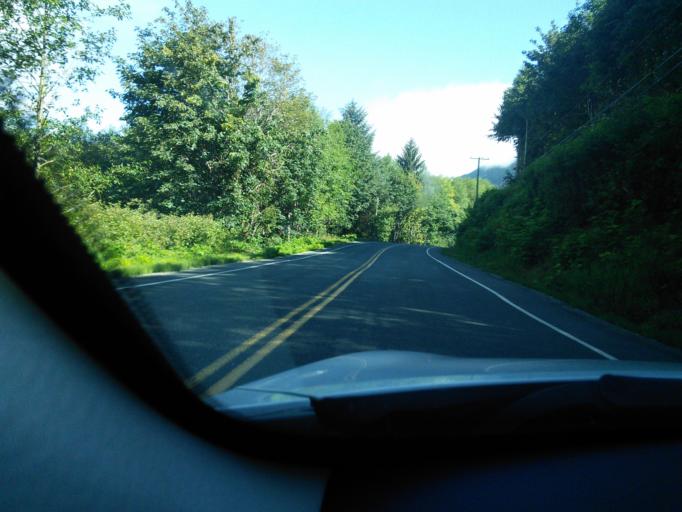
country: CA
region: British Columbia
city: Campbell River
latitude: 50.3437
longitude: -125.9069
